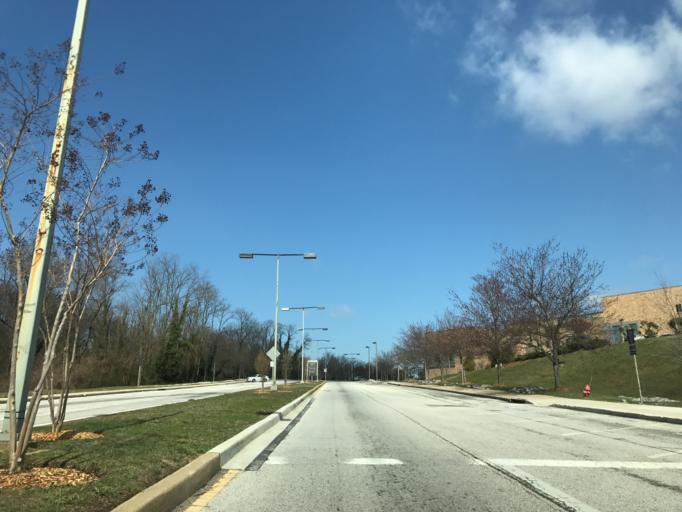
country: US
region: Maryland
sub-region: Baltimore County
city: Arbutus
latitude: 39.2539
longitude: -76.7154
